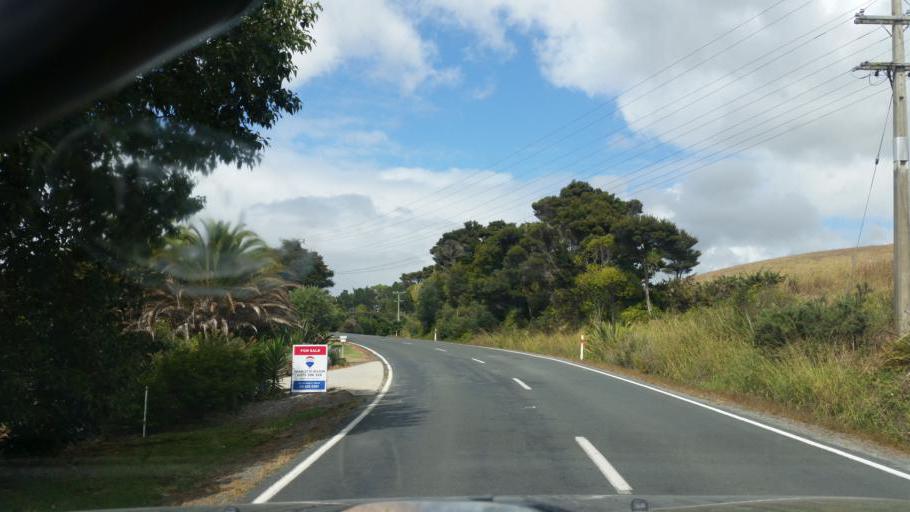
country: NZ
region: Auckland
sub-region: Auckland
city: Wellsford
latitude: -36.0845
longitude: 174.5702
